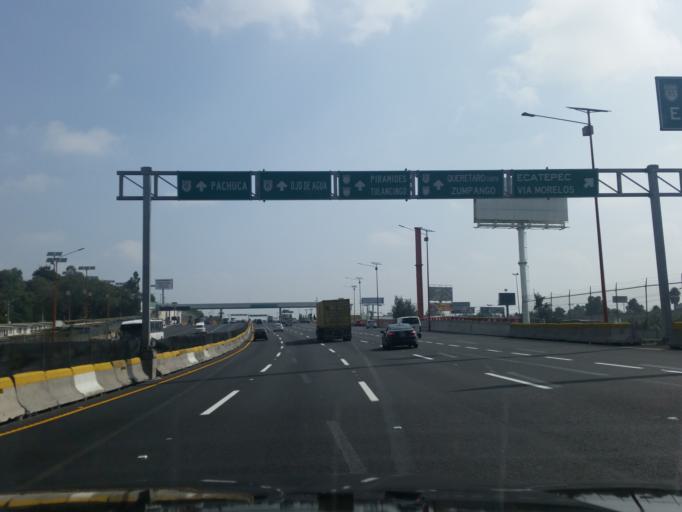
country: MX
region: Mexico
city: Ecatepec
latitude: 19.5842
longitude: -99.0429
